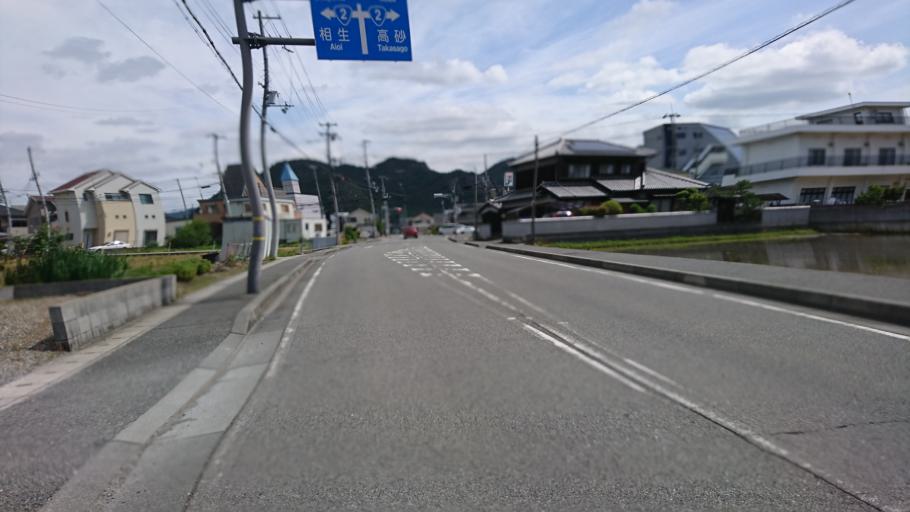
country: JP
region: Hyogo
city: Shirahamacho-usazakiminami
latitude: 34.8136
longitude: 134.7450
